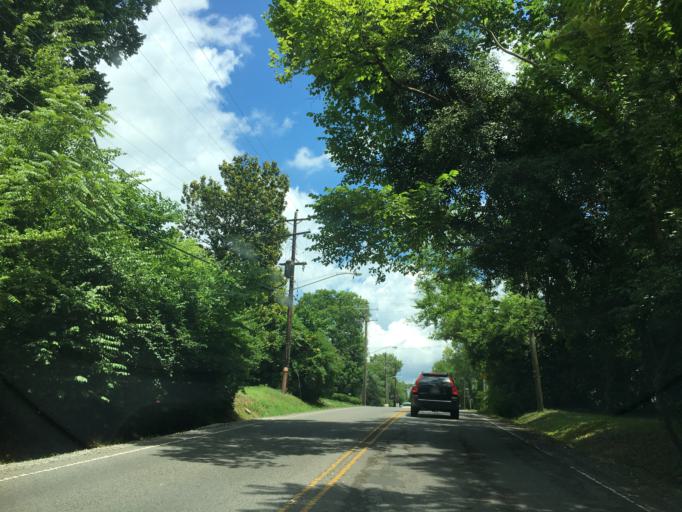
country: US
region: Tennessee
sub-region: Davidson County
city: Oak Hill
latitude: 36.0885
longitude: -86.7929
